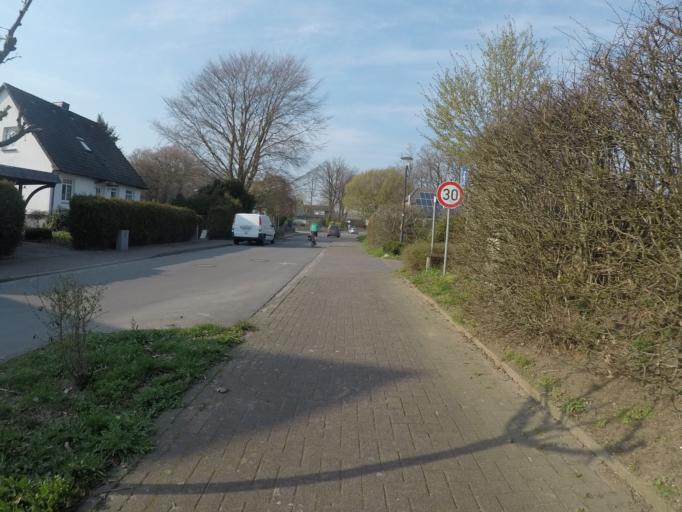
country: DE
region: Schleswig-Holstein
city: Wittenborn
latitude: 53.9206
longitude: 10.2213
